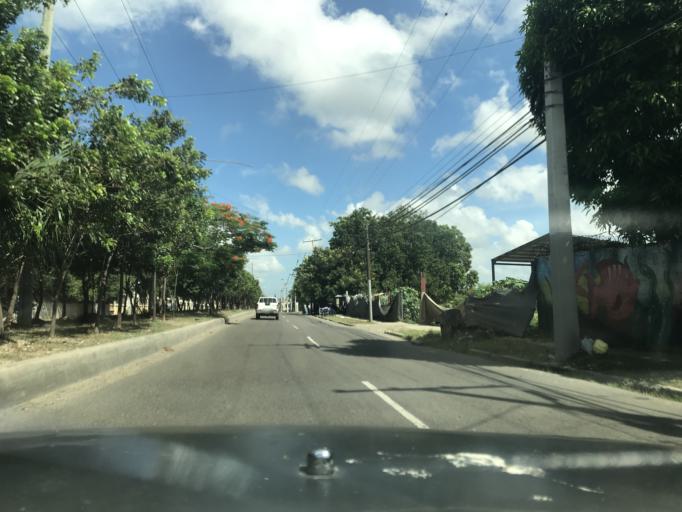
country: DO
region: Santiago
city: Santiago de los Caballeros
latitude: 19.4422
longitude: -70.7352
